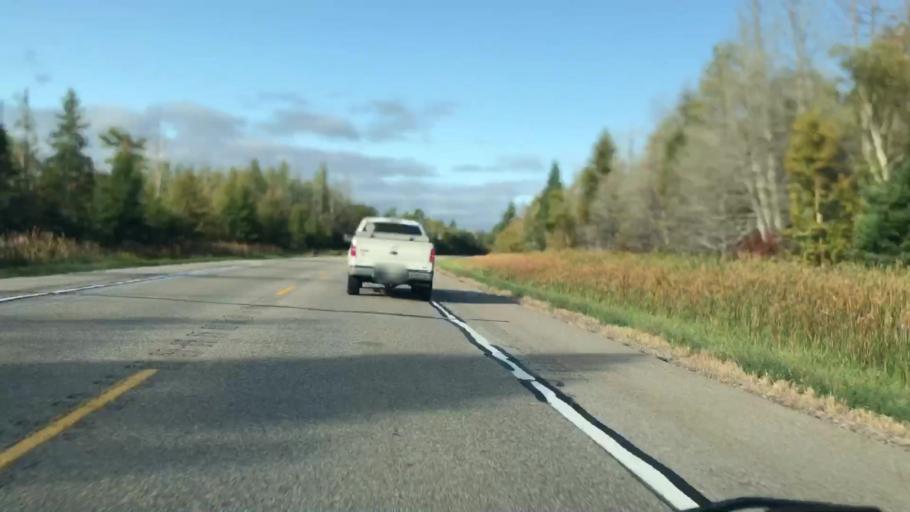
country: US
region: Michigan
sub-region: Luce County
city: Newberry
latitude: 46.3045
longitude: -85.2234
